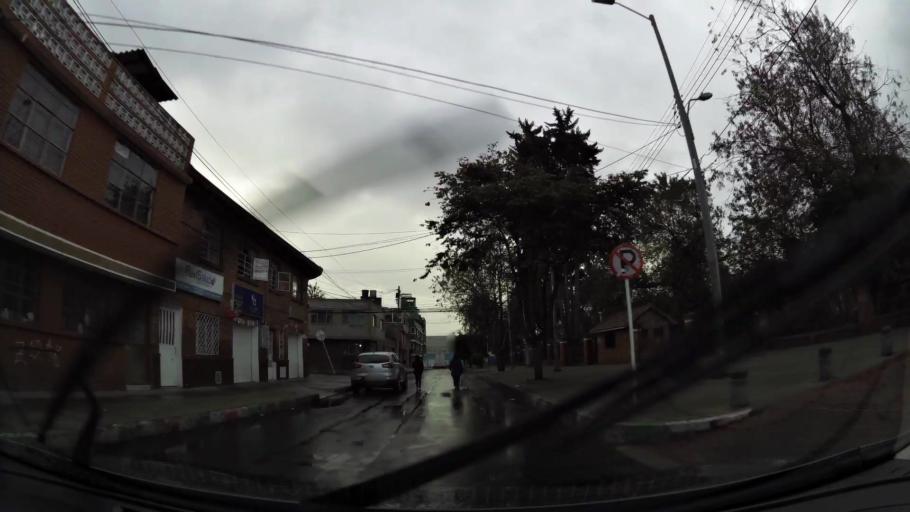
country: CO
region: Bogota D.C.
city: Barrio San Luis
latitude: 4.6757
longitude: -74.0804
